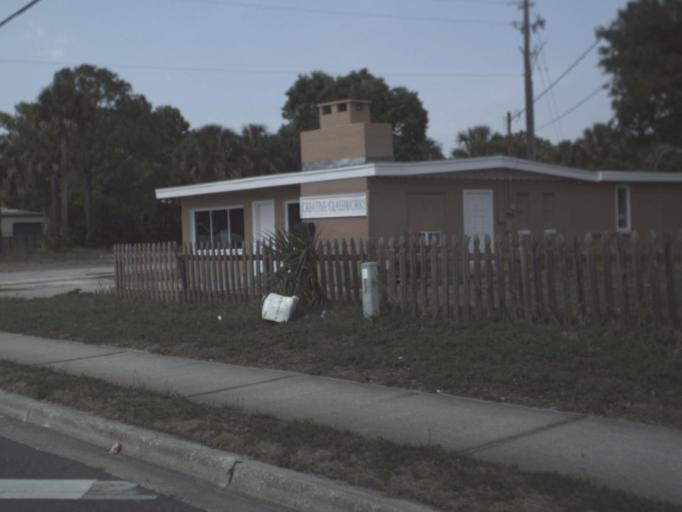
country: US
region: Florida
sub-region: Duval County
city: Atlantic Beach
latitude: 30.3402
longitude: -81.4132
